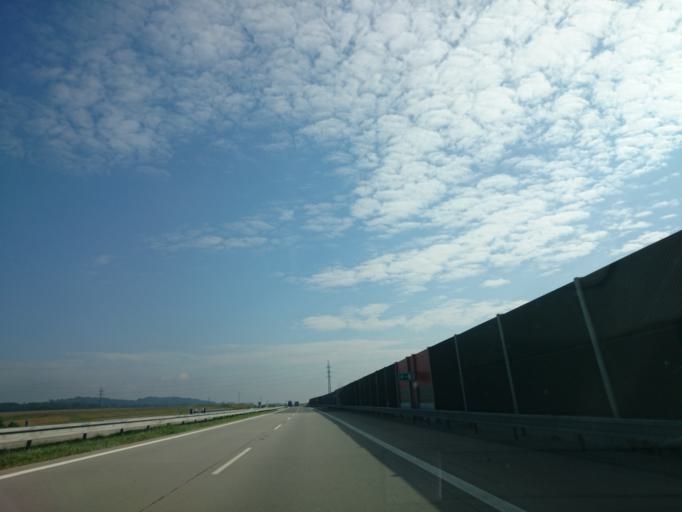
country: CZ
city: Bilovec
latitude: 49.7075
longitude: 17.9934
